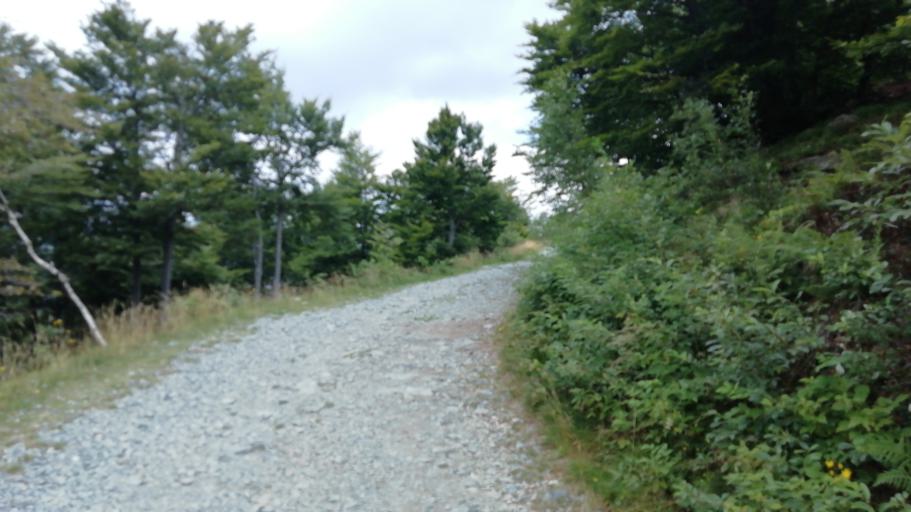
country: IT
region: Piedmont
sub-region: Provincia di Biella
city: Camandona
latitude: 45.6661
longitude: 8.0728
